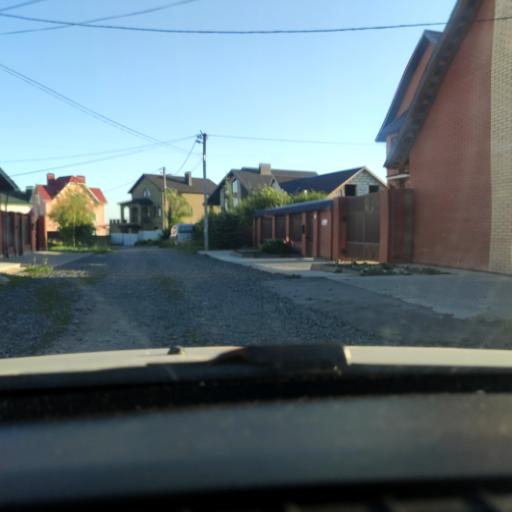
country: RU
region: Samara
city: Kinel'
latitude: 53.2745
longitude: 50.5905
